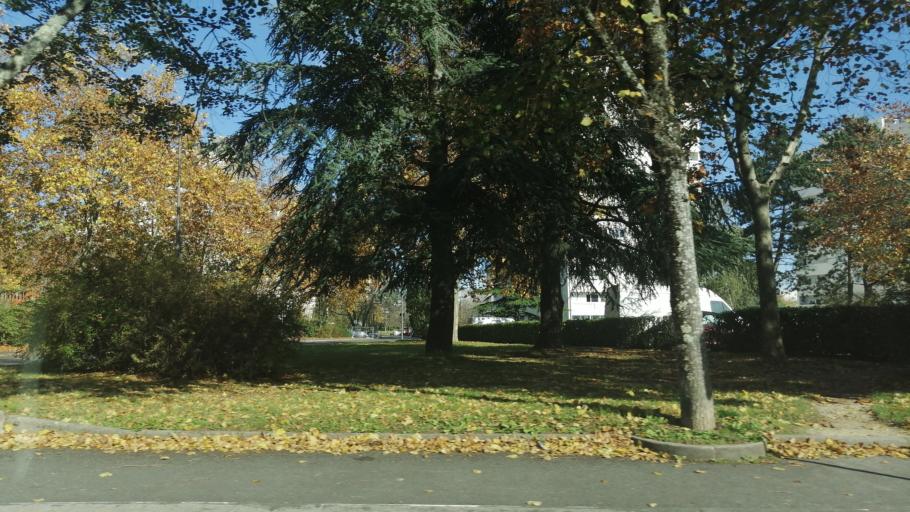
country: FR
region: Poitou-Charentes
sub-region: Departement de la Vienne
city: Poitiers
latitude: 46.5886
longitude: 0.3623
